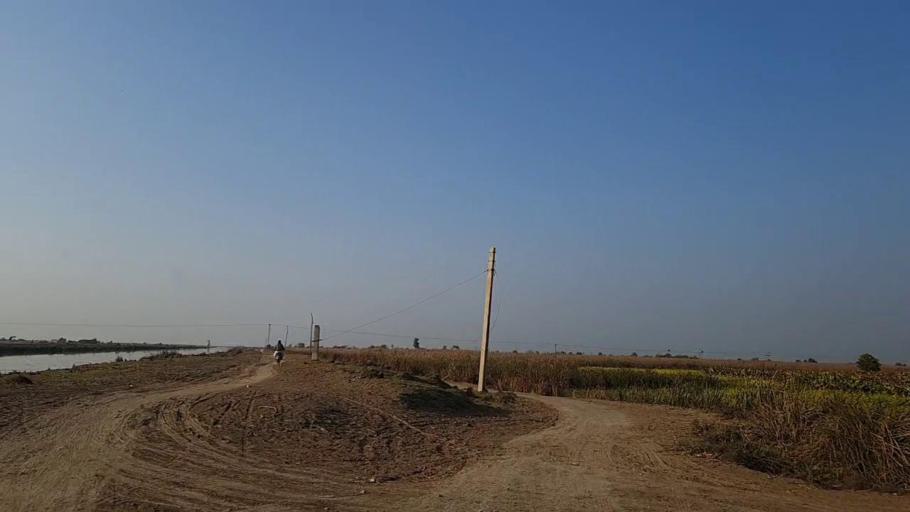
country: PK
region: Sindh
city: Sakrand
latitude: 26.0947
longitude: 68.3721
